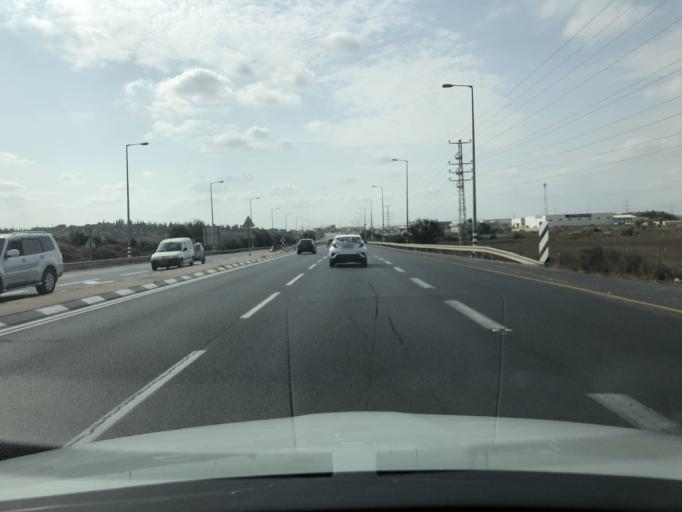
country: IL
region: Central District
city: Tirah
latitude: 32.2313
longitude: 34.9837
